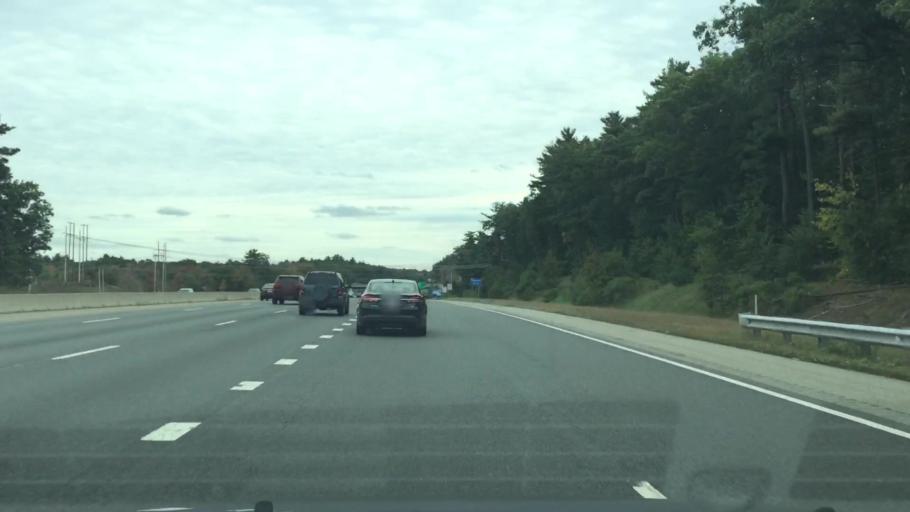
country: US
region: Massachusetts
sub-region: Middlesex County
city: Lowell
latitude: 42.5934
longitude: -71.3167
